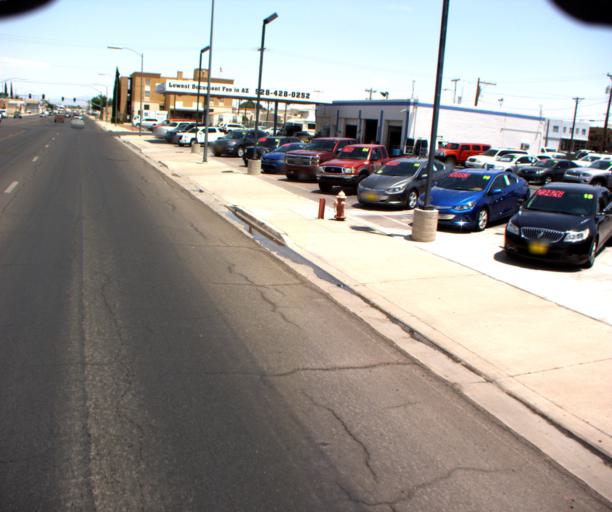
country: US
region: Arizona
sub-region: Graham County
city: Safford
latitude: 32.8343
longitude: -109.7147
